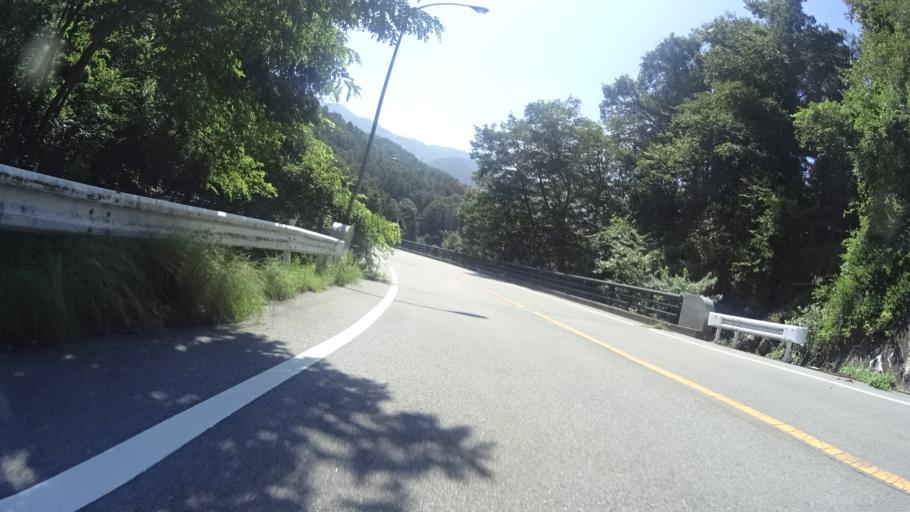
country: JP
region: Yamanashi
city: Enzan
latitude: 35.7488
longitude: 138.8064
